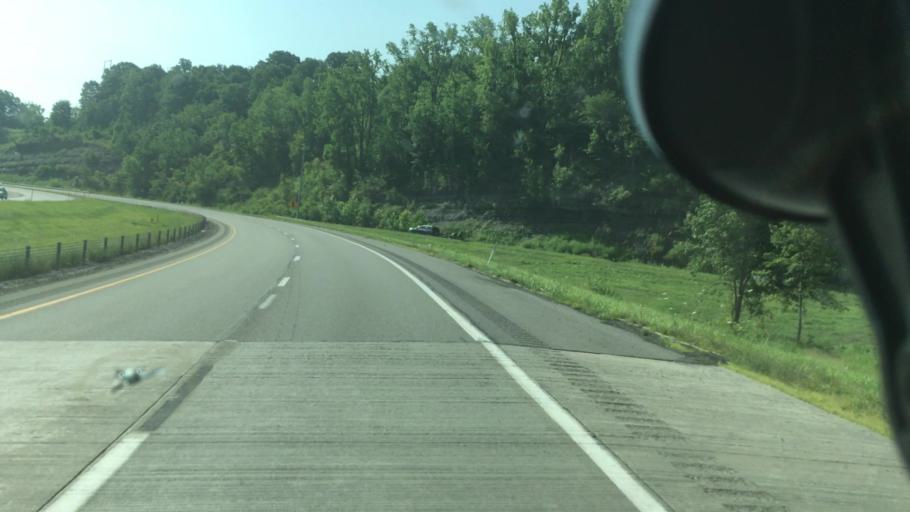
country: US
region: Pennsylvania
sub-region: Lawrence County
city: Oakland
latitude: 40.9687
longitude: -80.3644
